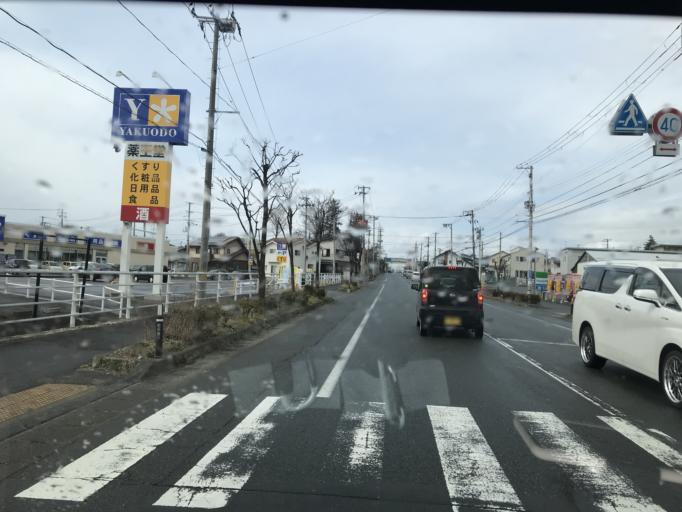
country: JP
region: Iwate
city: Kitakami
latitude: 39.2975
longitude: 141.1183
